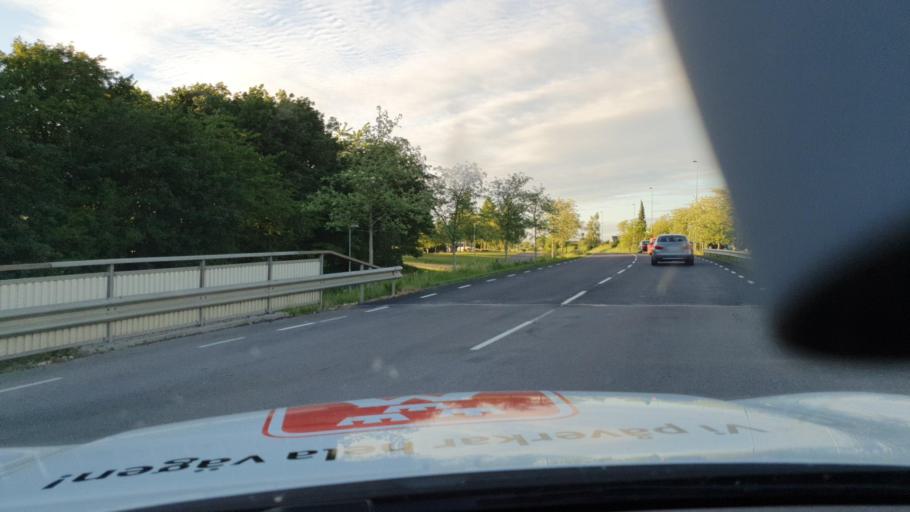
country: SE
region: Vaestra Goetaland
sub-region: Falkopings Kommun
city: Falkoeping
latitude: 58.1542
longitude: 13.5613
